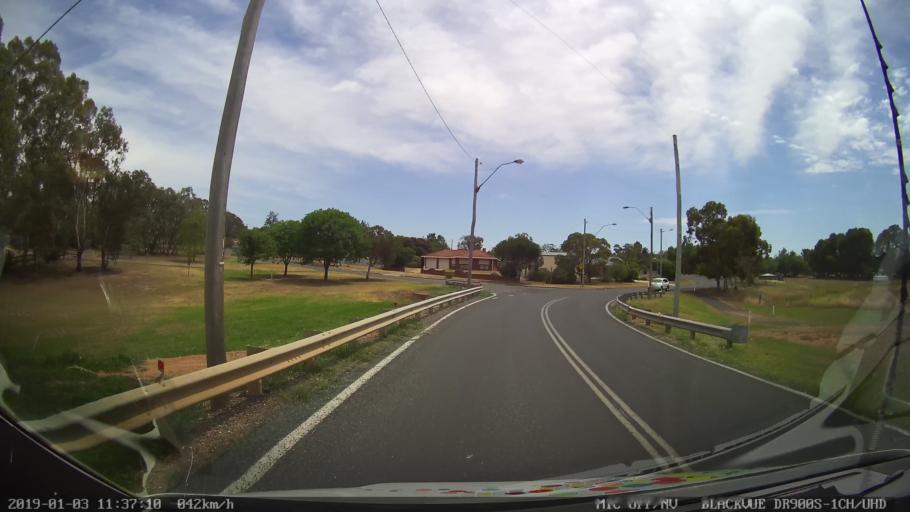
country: AU
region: New South Wales
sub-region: Weddin
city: Grenfell
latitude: -33.9046
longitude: 148.1605
